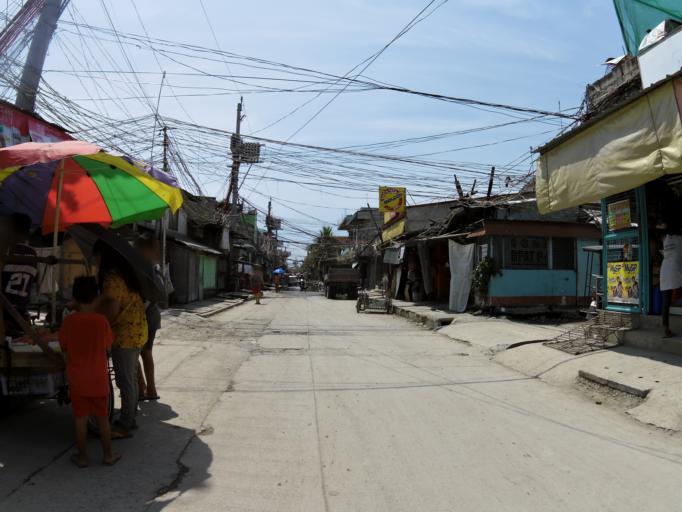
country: PH
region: Calabarzon
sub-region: Province of Rizal
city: Taguig
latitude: 14.5351
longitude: 121.1091
